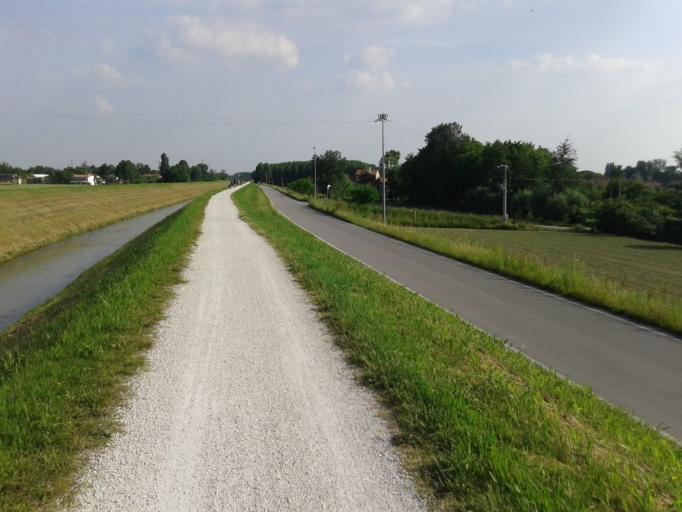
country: IT
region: Veneto
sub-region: Provincia di Padova
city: Loreggia
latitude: 45.5892
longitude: 11.9376
